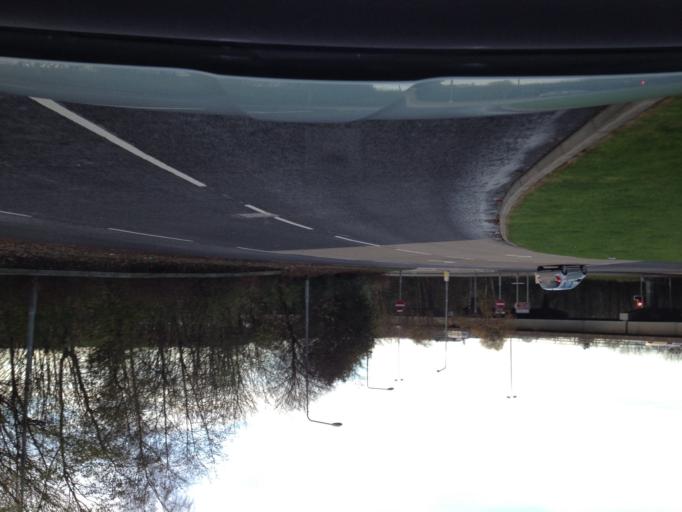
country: GB
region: Scotland
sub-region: West Lothian
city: Livingston
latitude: 55.8906
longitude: -3.5043
